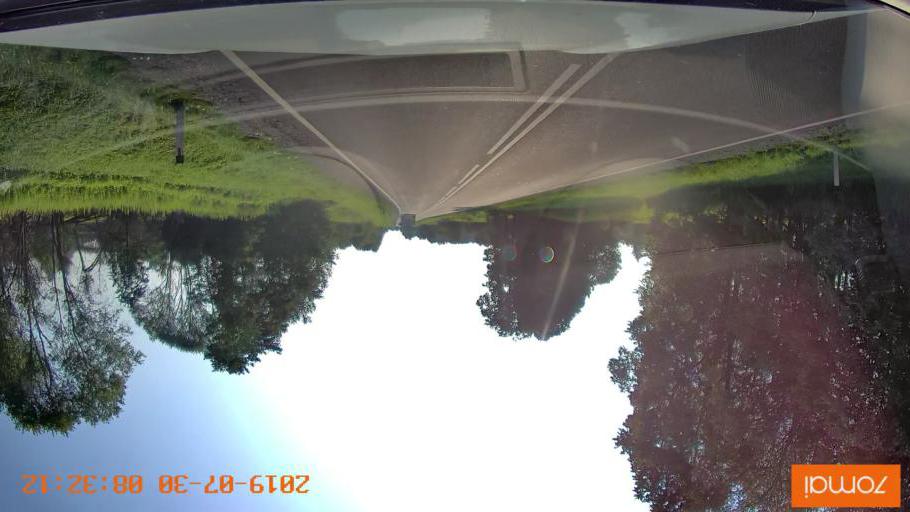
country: RU
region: Kaliningrad
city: Chernyakhovsk
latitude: 54.6382
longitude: 21.7245
